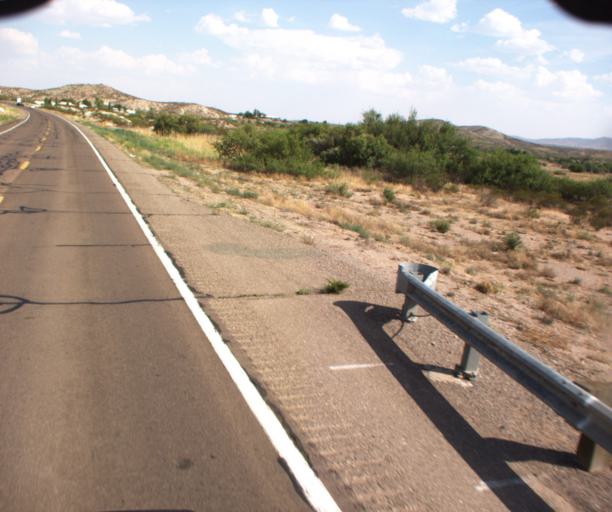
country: US
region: Arizona
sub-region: Greenlee County
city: Clifton
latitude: 32.7698
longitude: -109.1515
